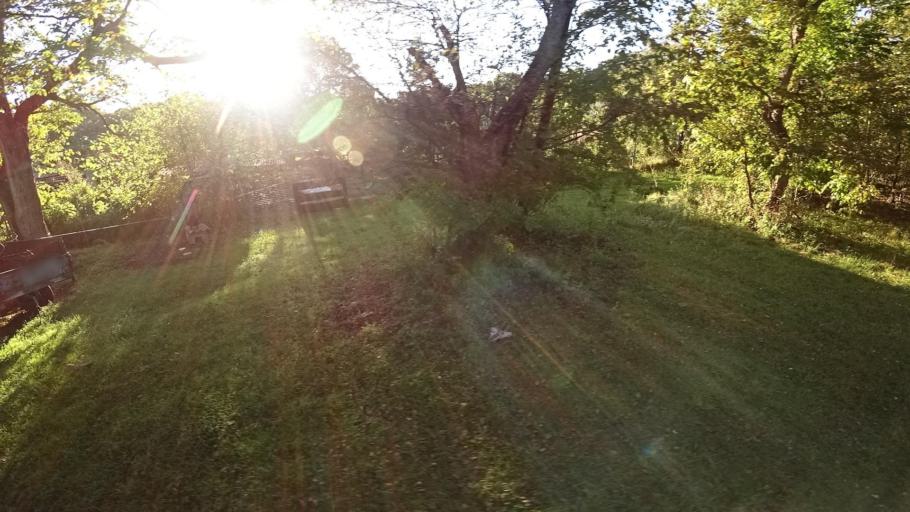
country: RU
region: Primorskiy
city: Kirovskiy
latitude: 44.8284
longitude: 133.5670
